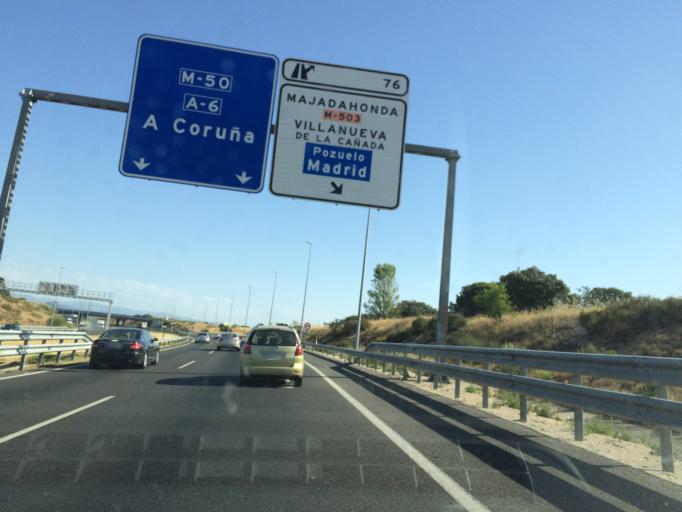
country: ES
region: Madrid
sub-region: Provincia de Madrid
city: Boadilla del Monte
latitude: 40.4388
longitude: -3.8775
